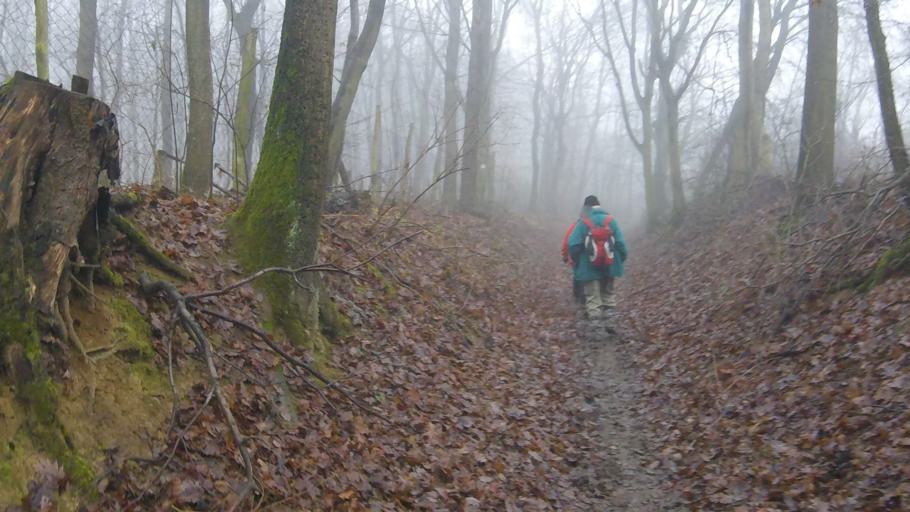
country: HU
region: Pest
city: Budakeszi
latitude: 47.5356
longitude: 18.9340
